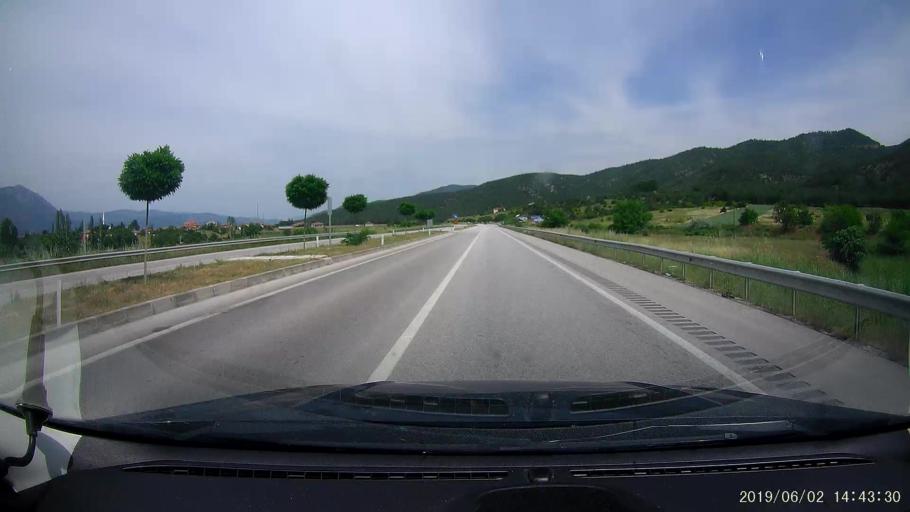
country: TR
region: Corum
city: Hacihamza
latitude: 41.0986
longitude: 34.3882
